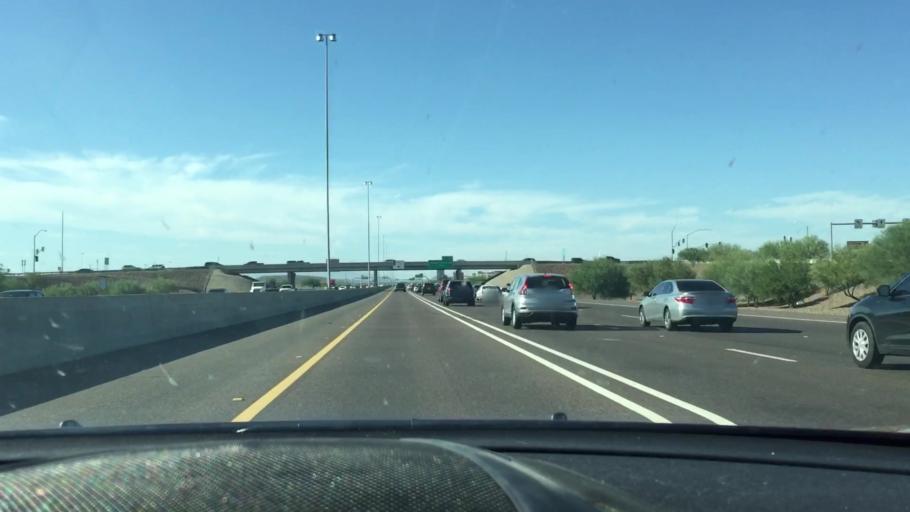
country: US
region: Arizona
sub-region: Maricopa County
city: Peoria
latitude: 33.6978
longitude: -112.1139
